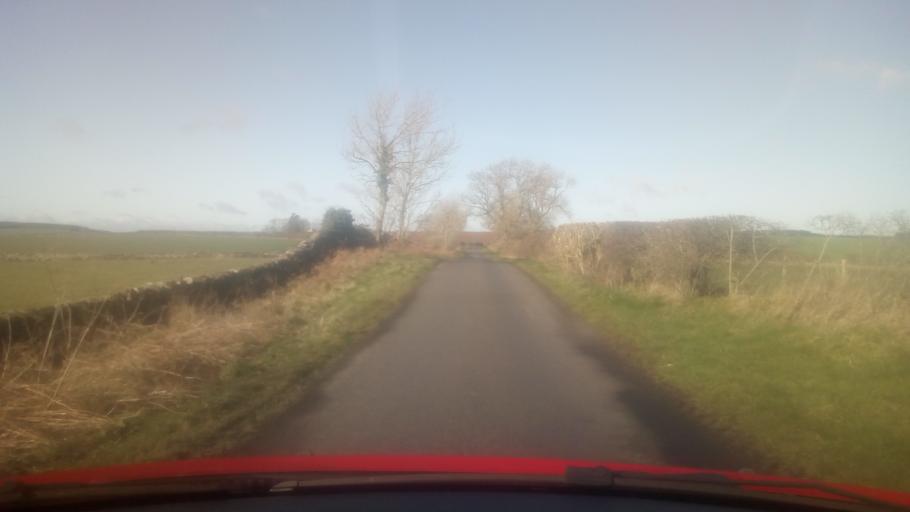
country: GB
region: Scotland
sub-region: The Scottish Borders
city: Jedburgh
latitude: 55.5217
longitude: -2.6023
